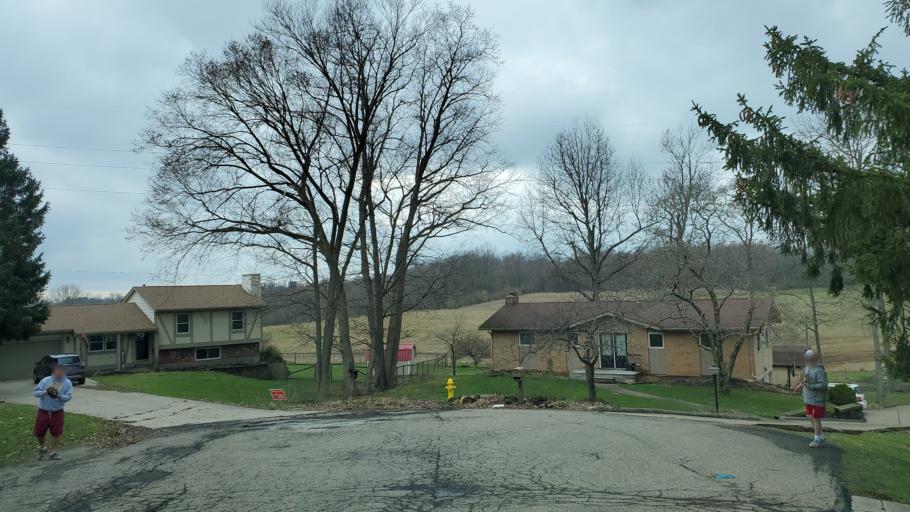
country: US
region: Ohio
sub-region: Licking County
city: Newark
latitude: 40.0286
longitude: -82.3821
